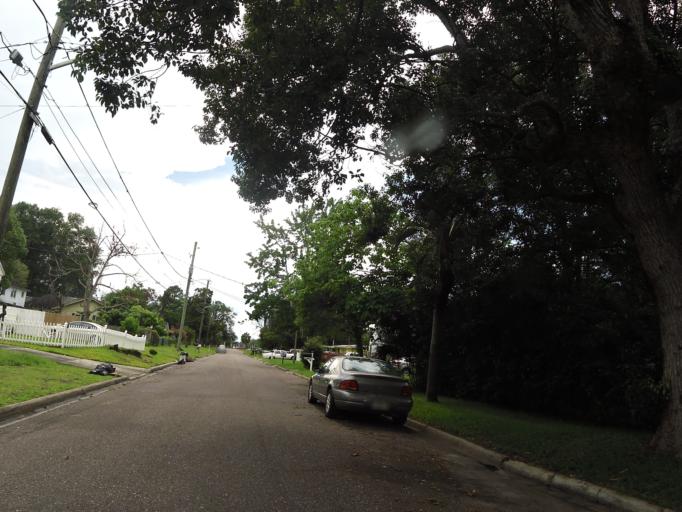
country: US
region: Florida
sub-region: Duval County
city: Jacksonville
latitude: 30.3719
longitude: -81.6486
